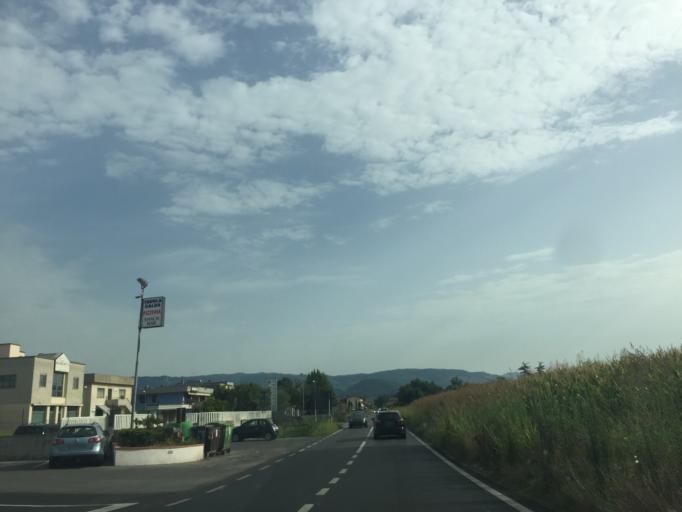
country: IT
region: Tuscany
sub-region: Provincia di Pistoia
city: Monsummano Terme
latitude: 43.8527
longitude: 10.7914
